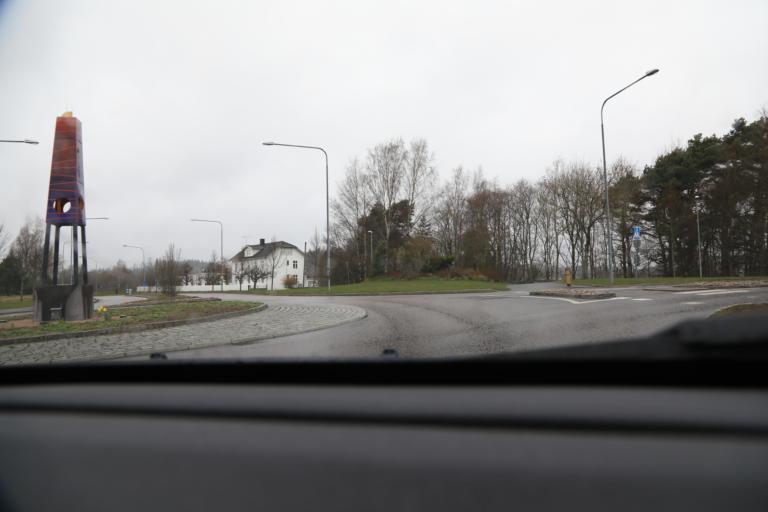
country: SE
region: Vaestra Goetaland
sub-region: Marks Kommun
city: Kinna
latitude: 57.5051
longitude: 12.6873
